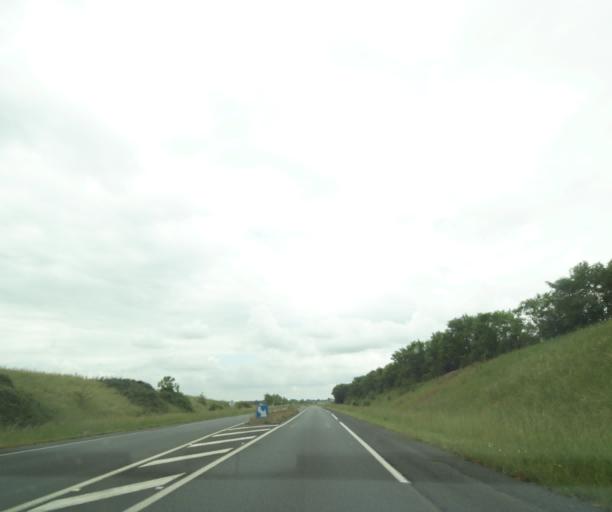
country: FR
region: Poitou-Charentes
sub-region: Departement des Deux-Sevres
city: Saint-Varent
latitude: 46.8882
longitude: -0.1940
